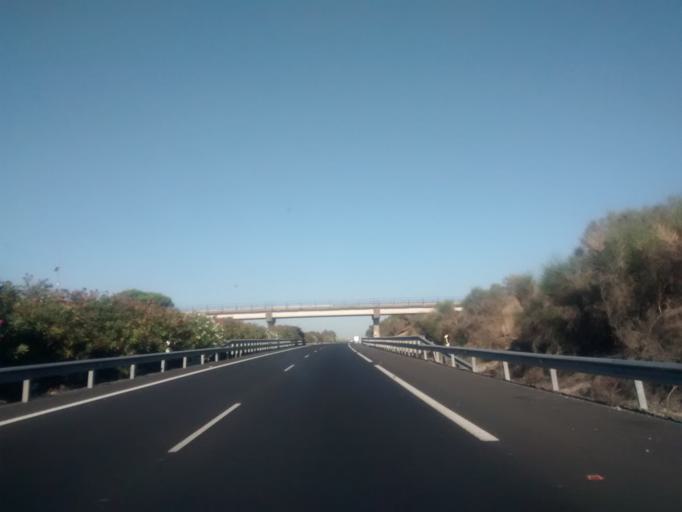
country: ES
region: Andalusia
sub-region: Provincia de Huelva
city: Chucena
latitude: 37.3537
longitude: -6.3699
